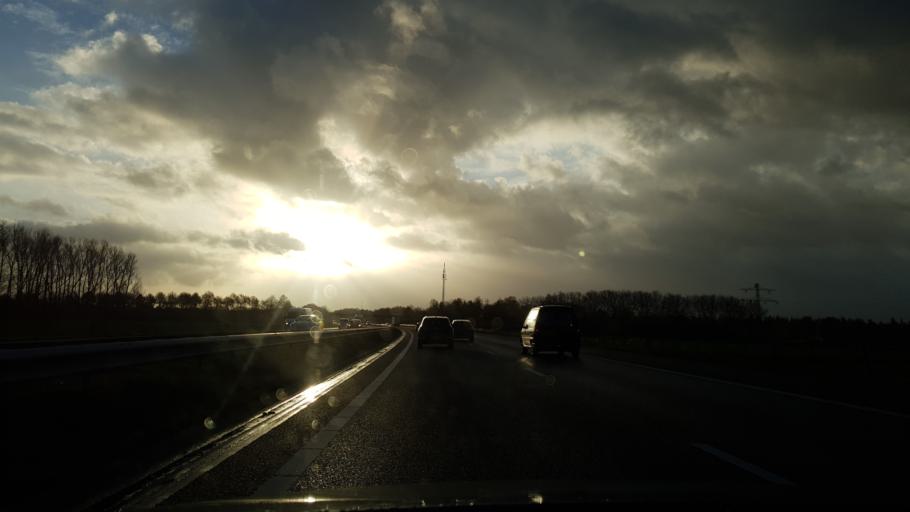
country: NL
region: North Brabant
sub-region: Gemeente Boxmeer
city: Boxmeer
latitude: 51.6158
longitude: 5.9361
